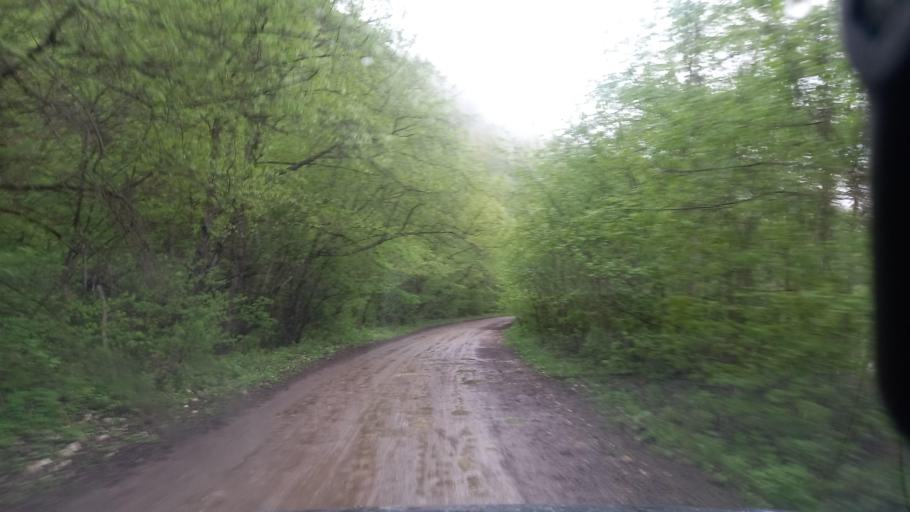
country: RU
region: Kabardino-Balkariya
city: Gundelen
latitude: 43.5784
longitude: 43.0997
